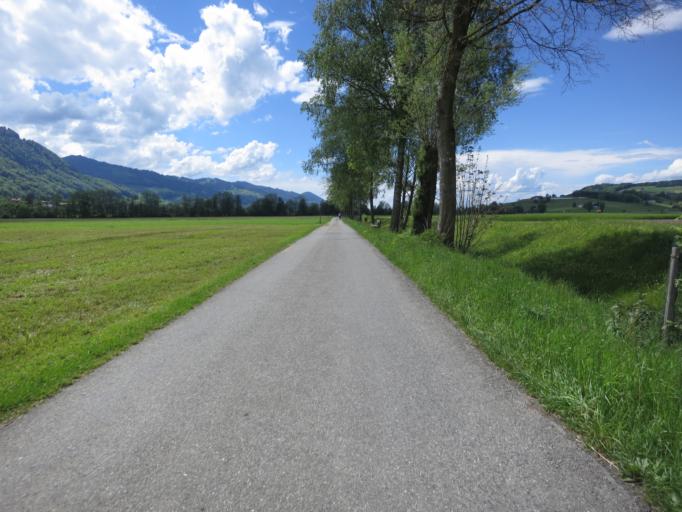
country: CH
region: Schwyz
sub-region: Bezirk March
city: Reichenburg
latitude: 47.1794
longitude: 8.9612
